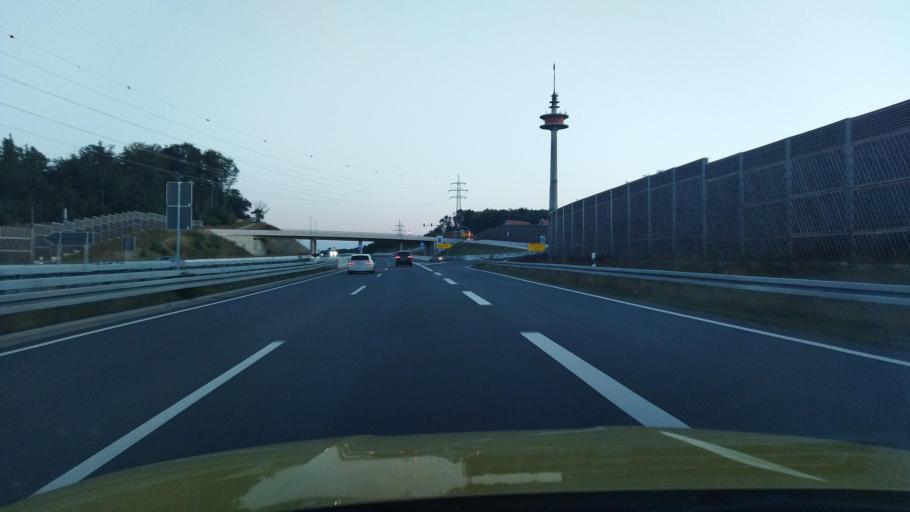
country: DE
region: Lower Saxony
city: Belm
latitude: 52.2998
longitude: 8.1079
